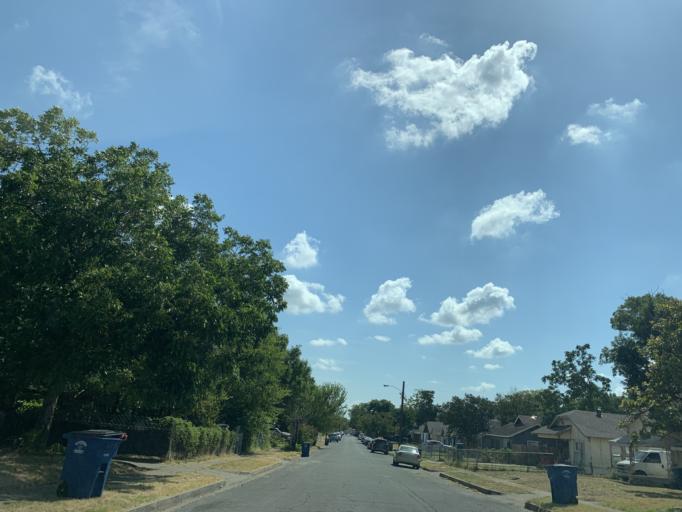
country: US
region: Texas
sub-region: Dallas County
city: Cockrell Hill
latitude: 32.7340
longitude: -96.8613
